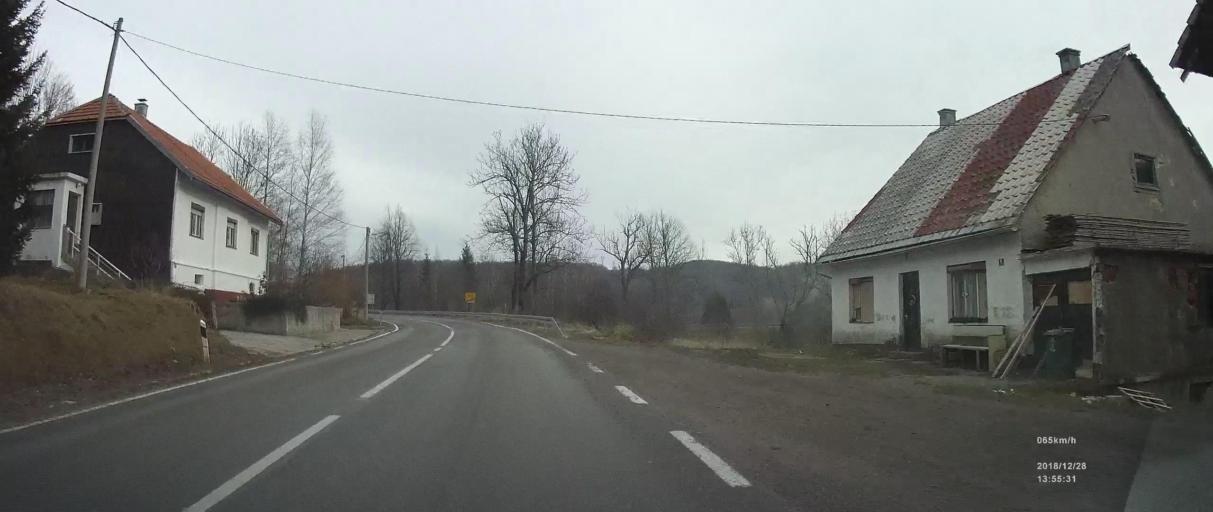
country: HR
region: Primorsko-Goranska
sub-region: Grad Delnice
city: Delnice
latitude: 45.3827
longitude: 14.8769
